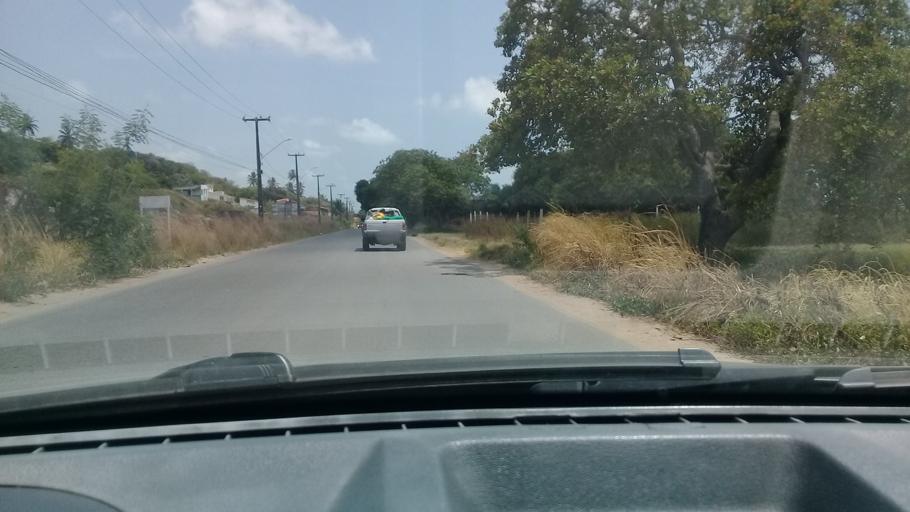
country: BR
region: Pernambuco
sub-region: Itamaraca
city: Itamaraca
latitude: -7.7817
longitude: -34.8368
